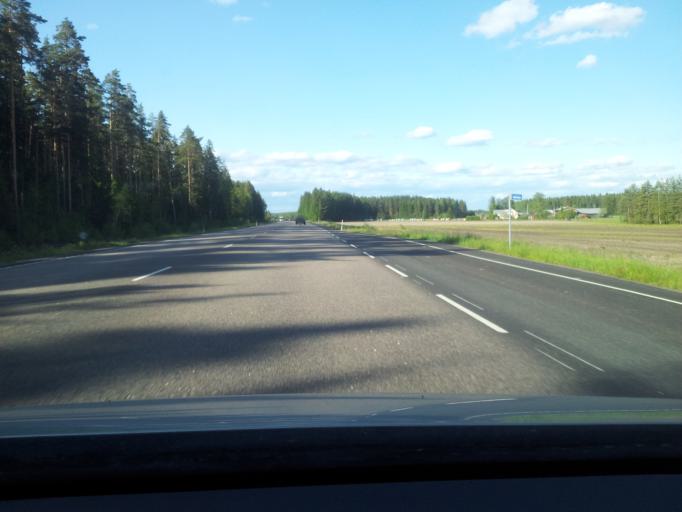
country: FI
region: Kymenlaakso
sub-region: Kouvola
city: Elimaeki
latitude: 60.7829
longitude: 26.4925
